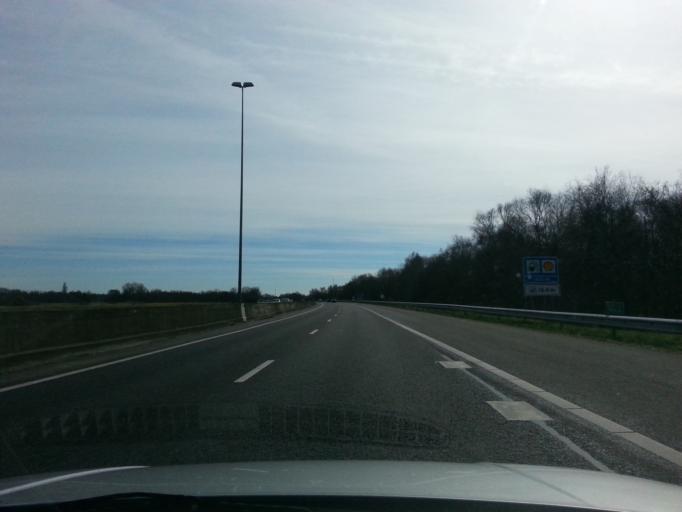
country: NL
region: Groningen
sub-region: Gemeente Haren
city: Haren
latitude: 53.1613
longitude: 6.5939
